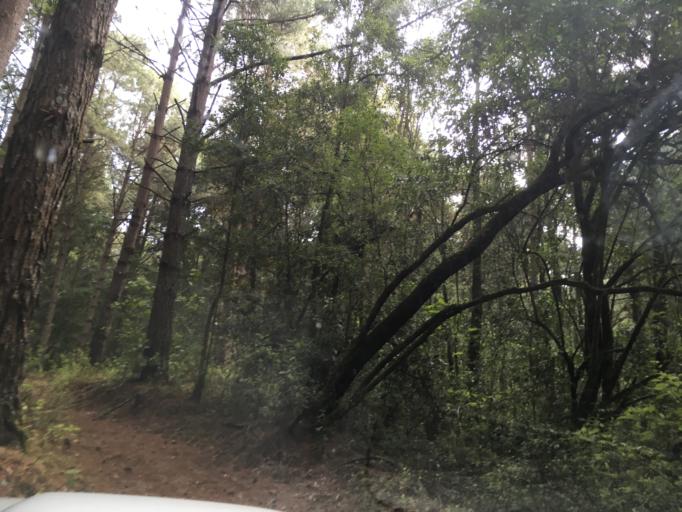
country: MX
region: Michoacan
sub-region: Zitacuaro
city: Francisco Serrato (San Bartolo)
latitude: 19.5211
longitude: -100.3068
